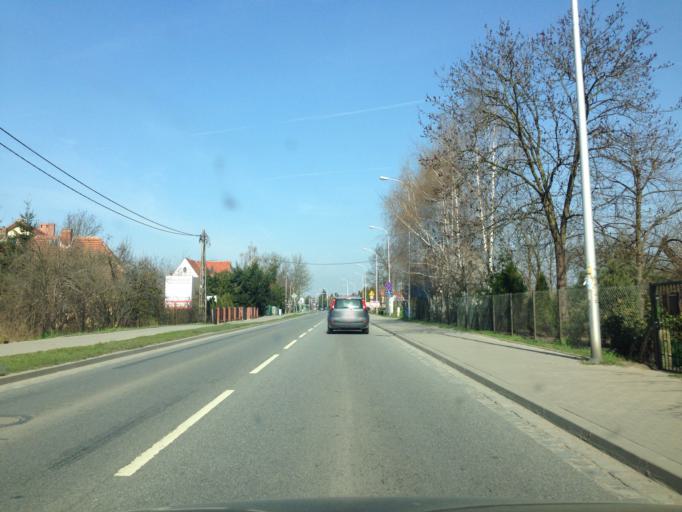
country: PL
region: Lower Silesian Voivodeship
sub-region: Powiat wroclawski
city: Wilczyce
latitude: 51.1017
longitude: 17.1573
